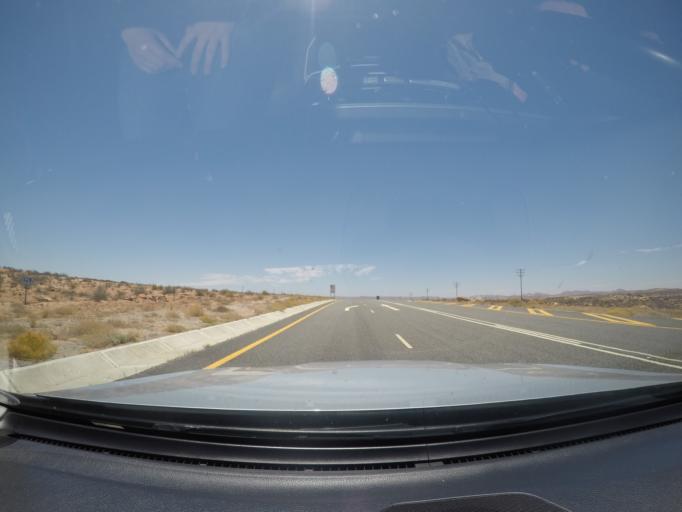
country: ZA
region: Northern Cape
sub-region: Namakwa District Municipality
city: Springbok
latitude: -29.3823
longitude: 17.7994
